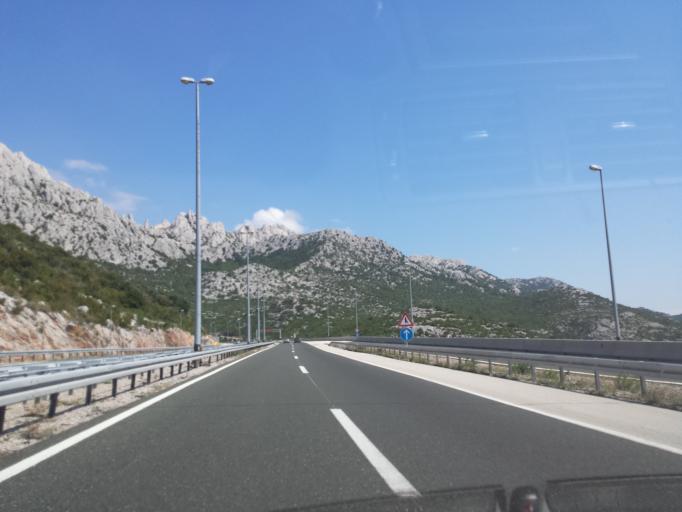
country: HR
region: Zadarska
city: Obrovac
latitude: 44.2520
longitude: 15.6412
